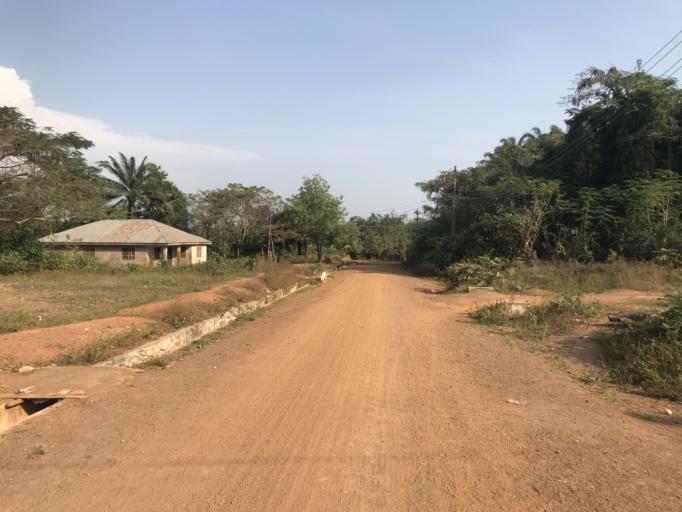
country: NG
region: Osun
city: Inisa
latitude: 7.8034
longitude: 4.2819
